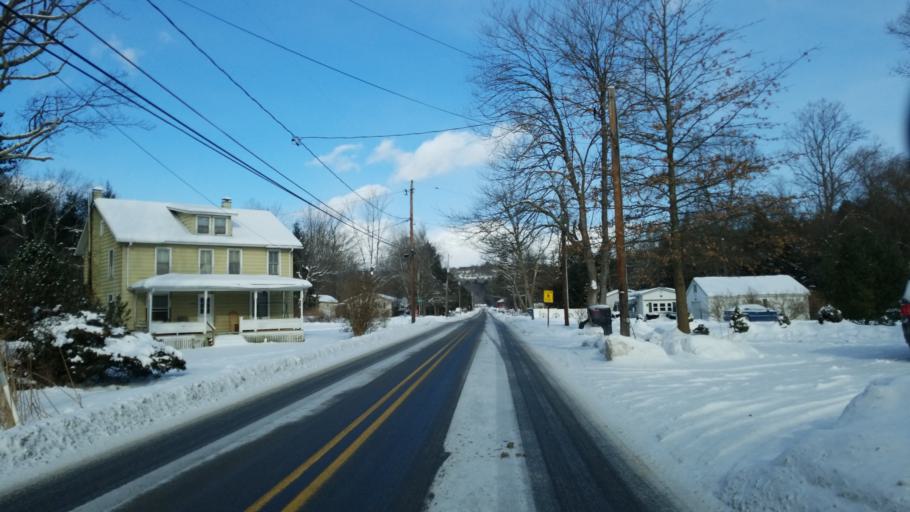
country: US
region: Pennsylvania
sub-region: Clearfield County
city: Hyde
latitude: 41.0049
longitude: -78.4674
